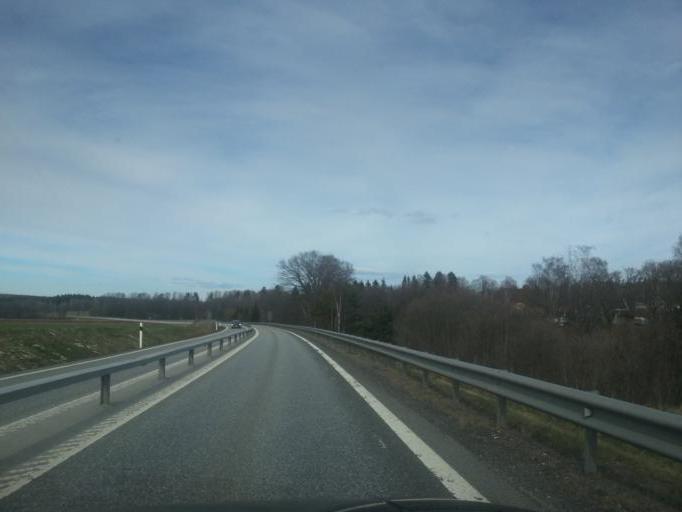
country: SE
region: Joenkoeping
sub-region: Jonkopings Kommun
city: Bankeryd
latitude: 57.8402
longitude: 14.1062
